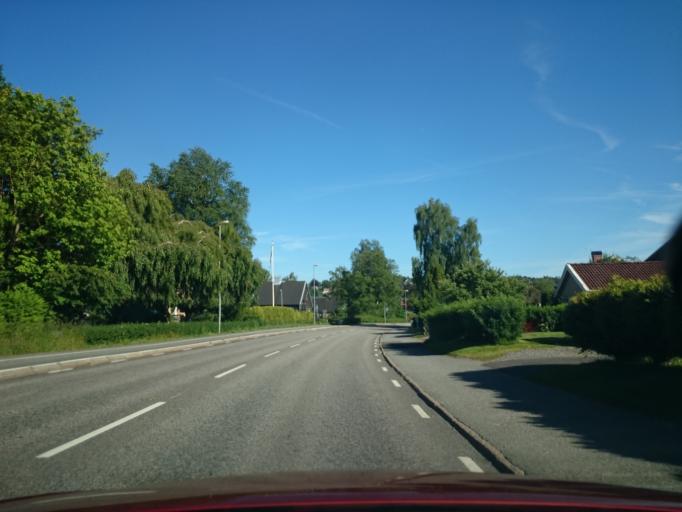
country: SE
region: Vaestra Goetaland
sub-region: Lerums Kommun
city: Lerum
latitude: 57.7749
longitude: 12.2654
